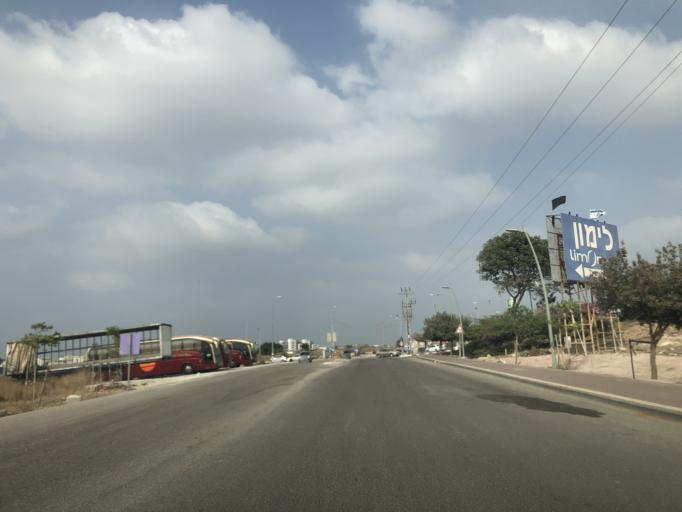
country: IL
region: Central District
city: Rosh Ha'Ayin
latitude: 32.0885
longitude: 34.9427
